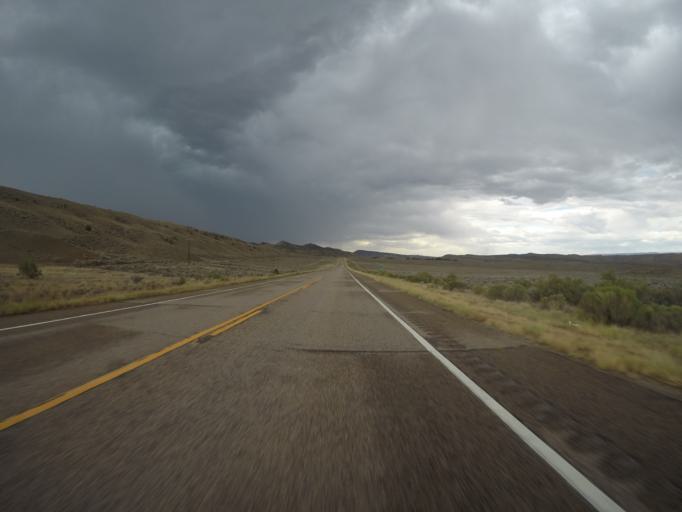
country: US
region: Colorado
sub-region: Rio Blanco County
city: Rangely
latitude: 40.2463
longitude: -108.8810
